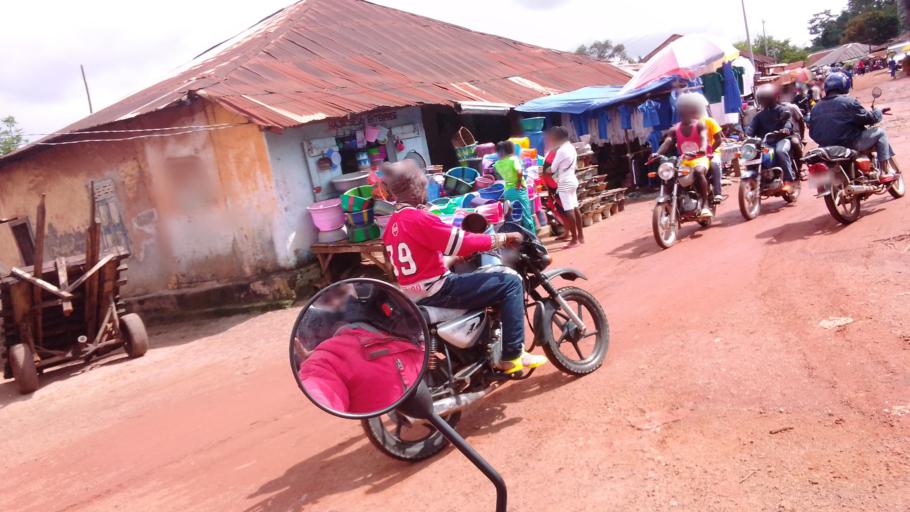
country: SL
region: Northern Province
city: Makeni
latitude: 8.8897
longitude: -12.0423
